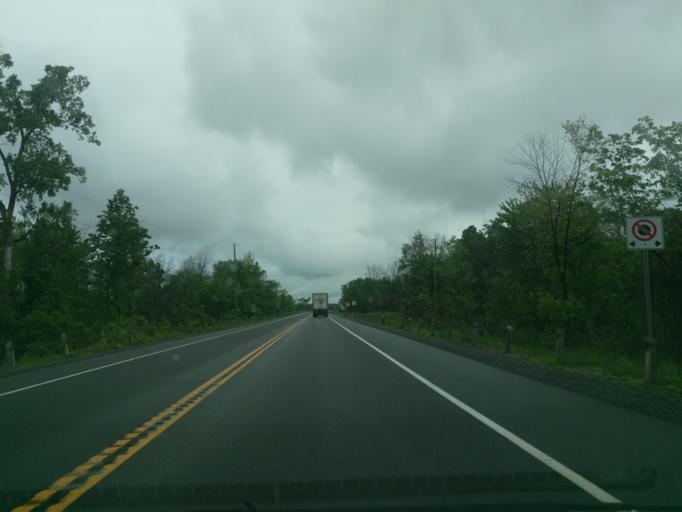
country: CA
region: Ontario
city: Clarence-Rockland
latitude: 45.5040
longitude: -75.4748
